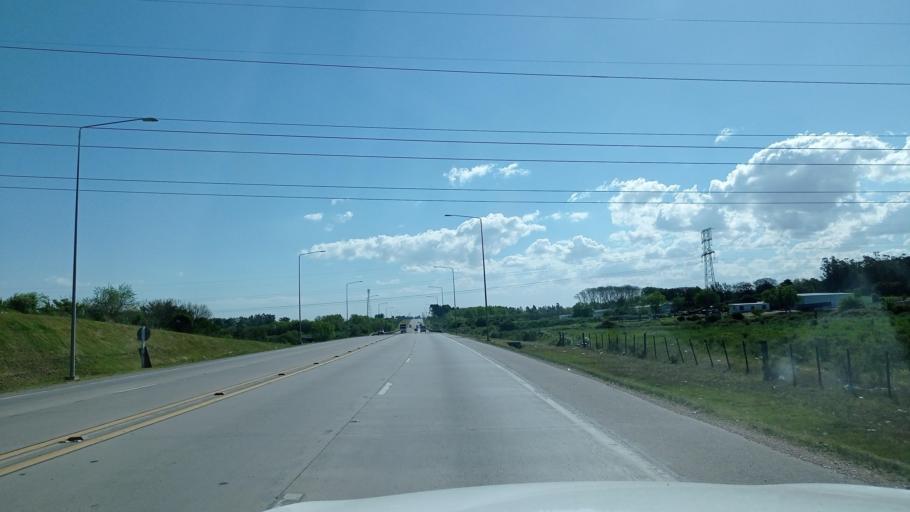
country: UY
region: Canelones
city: La Paz
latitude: -34.7940
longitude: -56.1804
